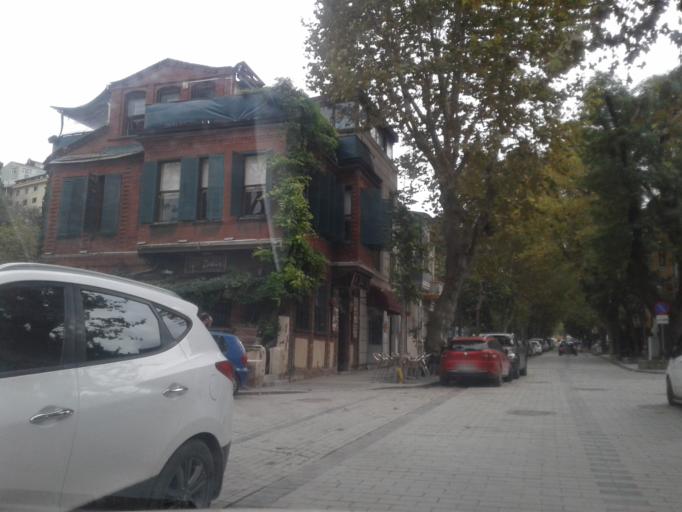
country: TR
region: Istanbul
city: UEskuedar
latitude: 41.0347
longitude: 29.0308
